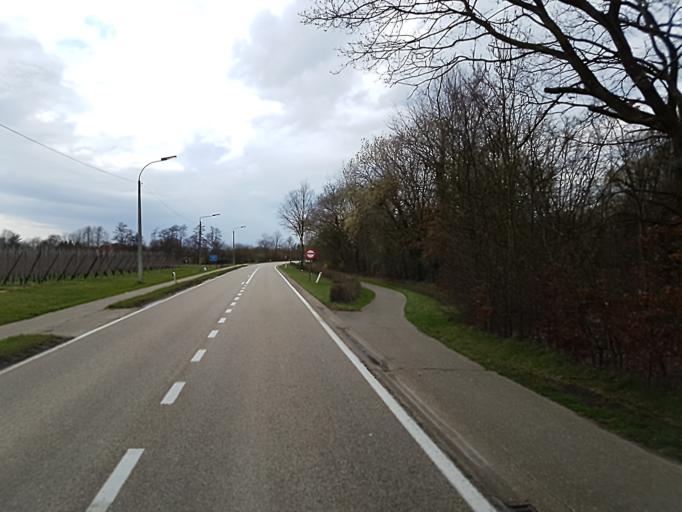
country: BE
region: Flanders
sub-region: Provincie Limburg
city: Herk-de-Stad
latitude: 50.9247
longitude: 5.2087
